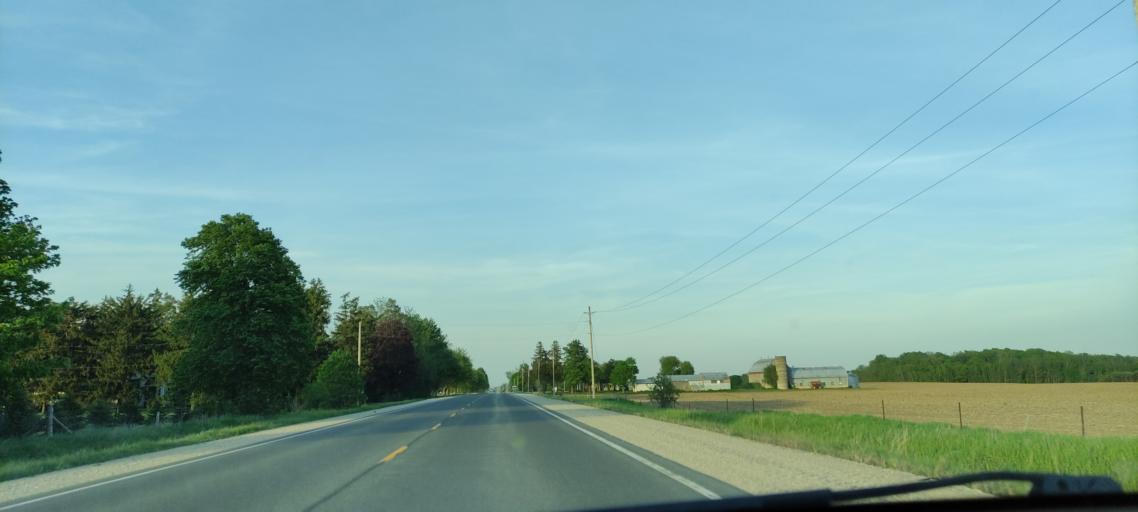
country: CA
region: Ontario
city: London
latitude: 43.2173
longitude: -81.1780
